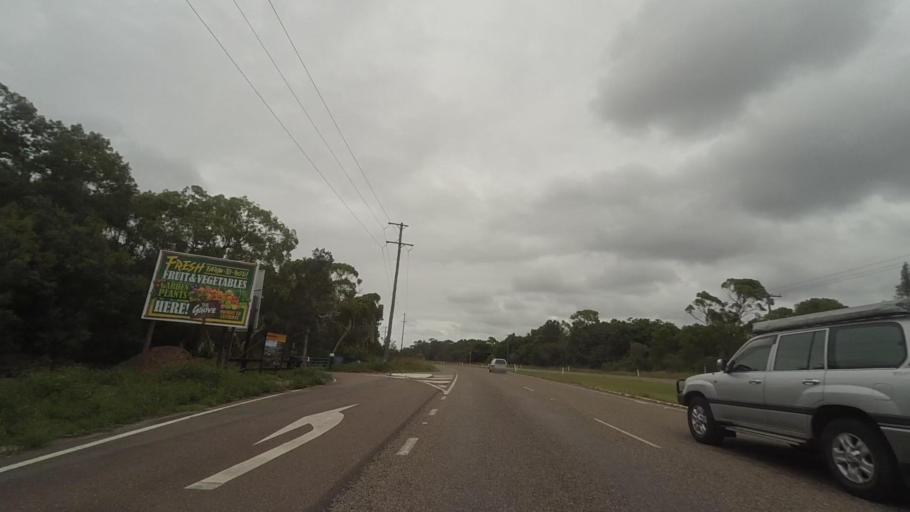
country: AU
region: New South Wales
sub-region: Wyong Shire
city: Buff Point
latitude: -33.1907
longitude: 151.5282
